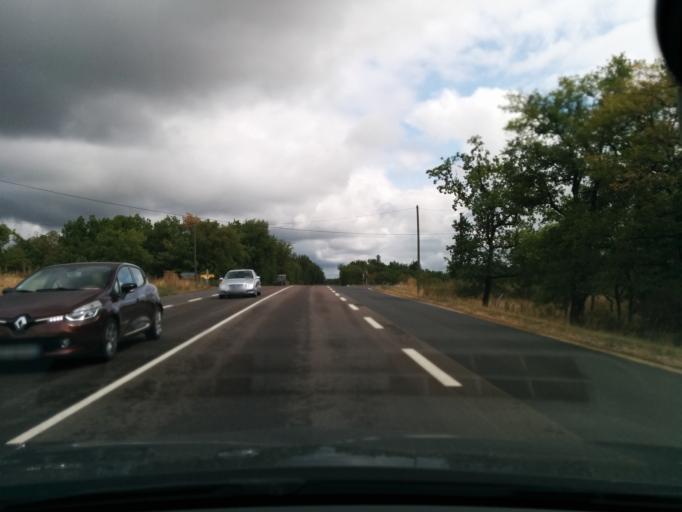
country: FR
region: Midi-Pyrenees
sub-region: Departement du Lot
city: Souillac
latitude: 44.9570
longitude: 1.4998
